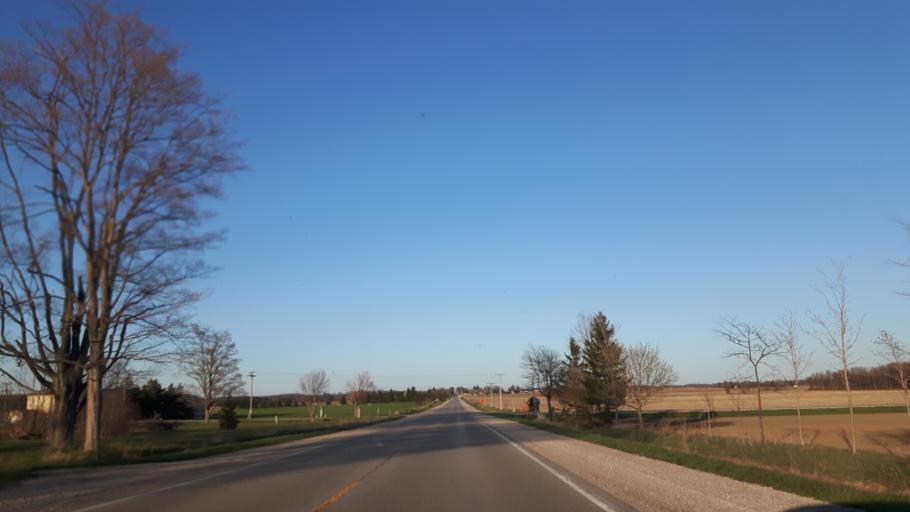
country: CA
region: Ontario
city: Bluewater
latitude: 43.5226
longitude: -81.5442
